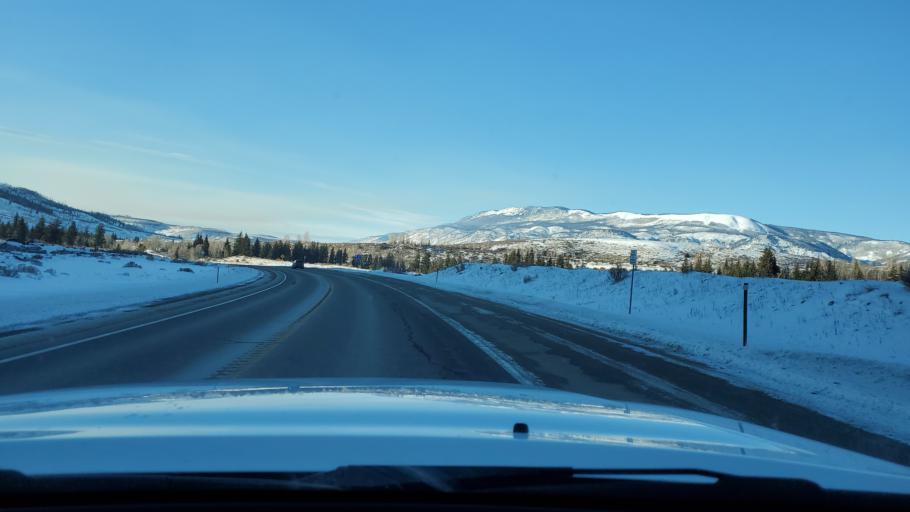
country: US
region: Colorado
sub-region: Summit County
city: Silverthorne
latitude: 39.7564
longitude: -106.1324
